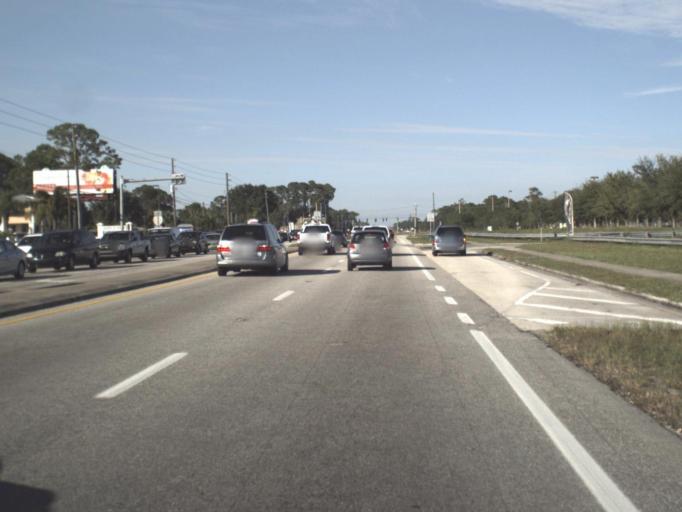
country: US
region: Florida
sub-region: Brevard County
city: June Park
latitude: 28.0359
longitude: -80.6714
